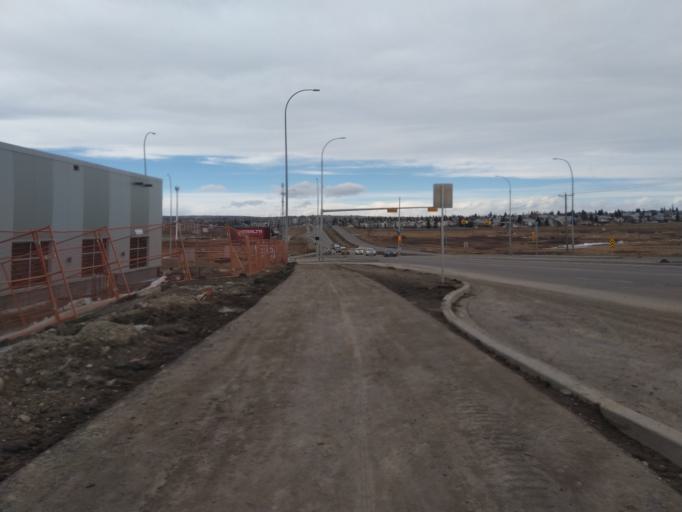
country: CA
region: Alberta
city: Calgary
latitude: 51.1541
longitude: -114.0308
